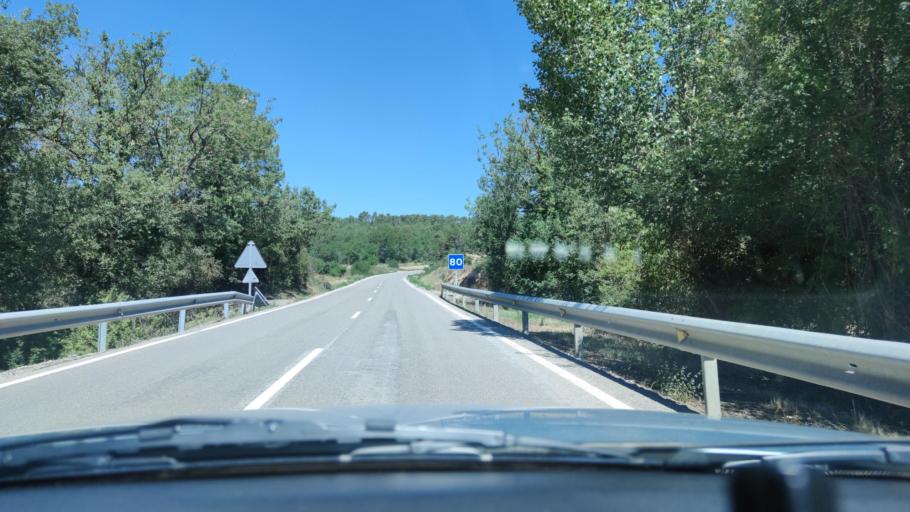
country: ES
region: Catalonia
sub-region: Provincia de Lleida
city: Solsona
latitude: 41.8914
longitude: 1.5638
